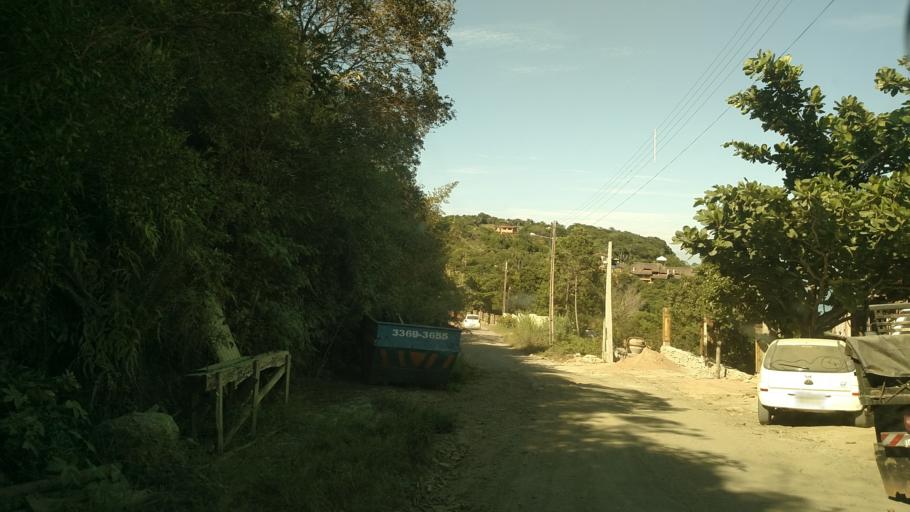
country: BR
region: Santa Catarina
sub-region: Porto Belo
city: Porto Belo
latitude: -27.2122
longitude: -48.5090
